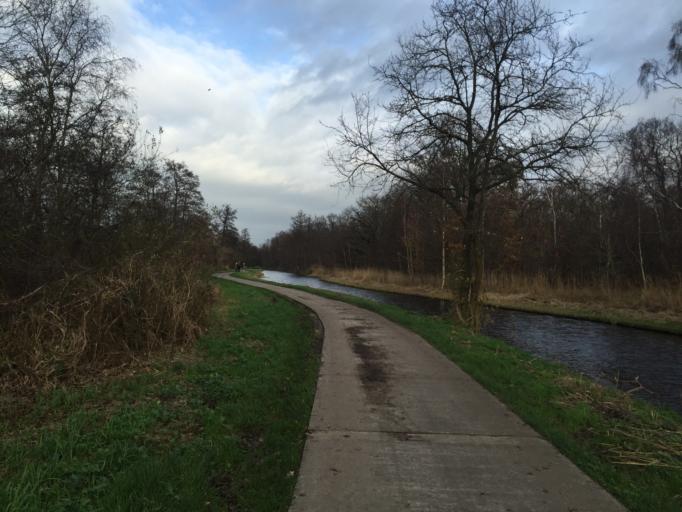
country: NL
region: North Holland
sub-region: Gemeente Wijdemeren
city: Kortenhoef
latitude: 52.2664
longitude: 5.0683
